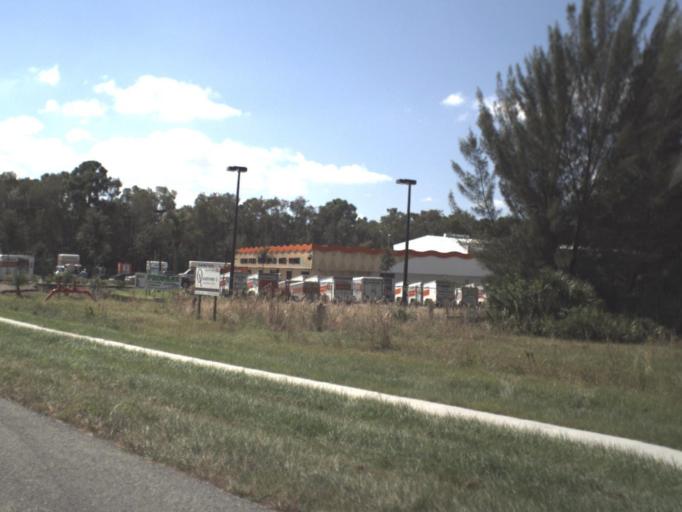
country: US
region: Florida
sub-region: Lee County
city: Palmona Park
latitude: 26.7109
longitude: -81.9021
